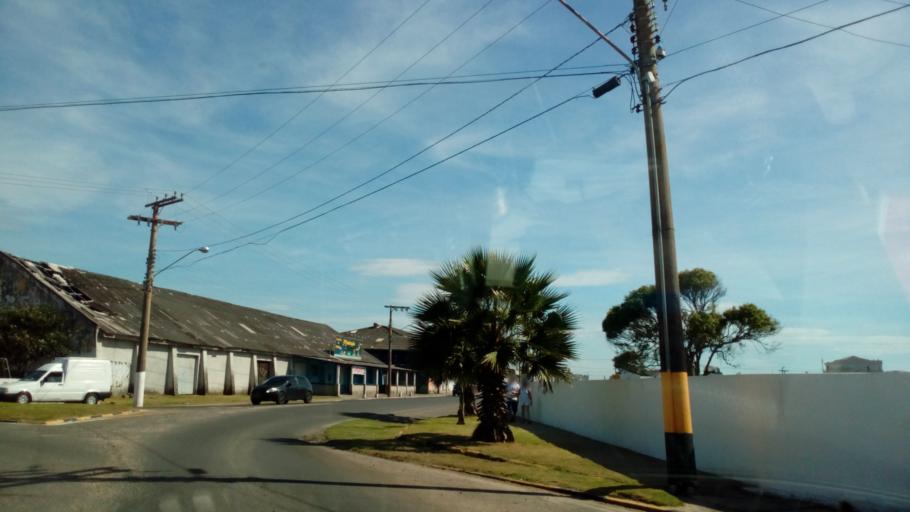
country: BR
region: Santa Catarina
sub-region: Laguna
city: Laguna
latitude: -28.4954
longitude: -48.7736
